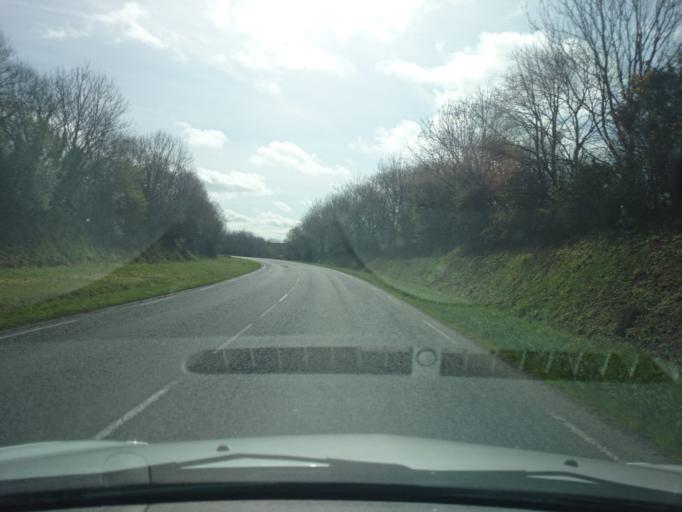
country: FR
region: Brittany
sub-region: Departement du Finistere
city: Gouesnou
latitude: 48.4397
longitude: -4.4562
